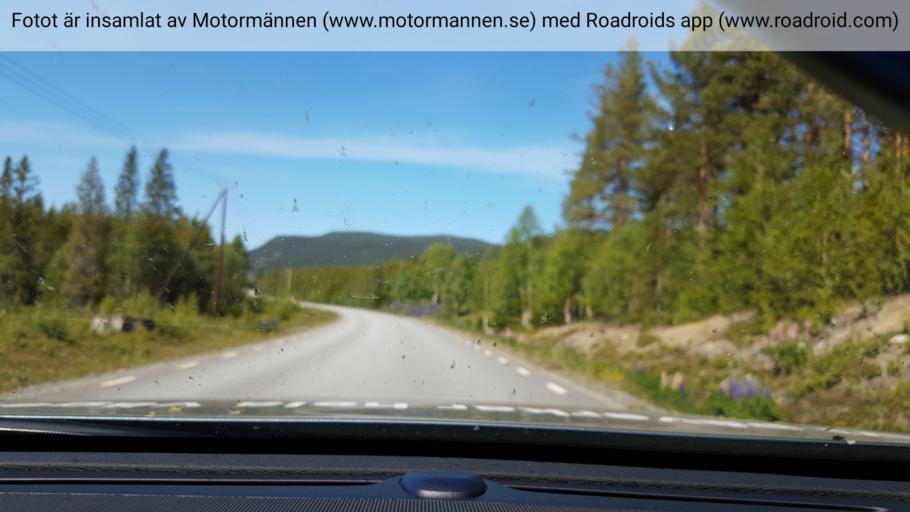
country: SE
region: Vaesterbotten
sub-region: Vilhelmina Kommun
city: Sjoberg
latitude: 64.7090
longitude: 15.5188
